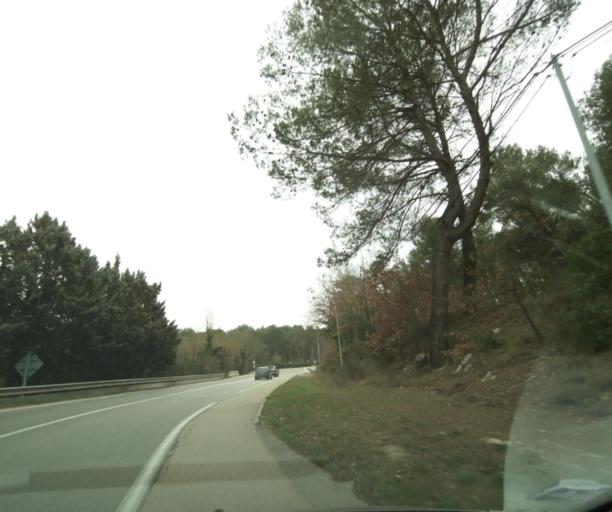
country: FR
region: Provence-Alpes-Cote d'Azur
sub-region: Departement des Bouches-du-Rhone
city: Fuveau
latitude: 43.4610
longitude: 5.5472
